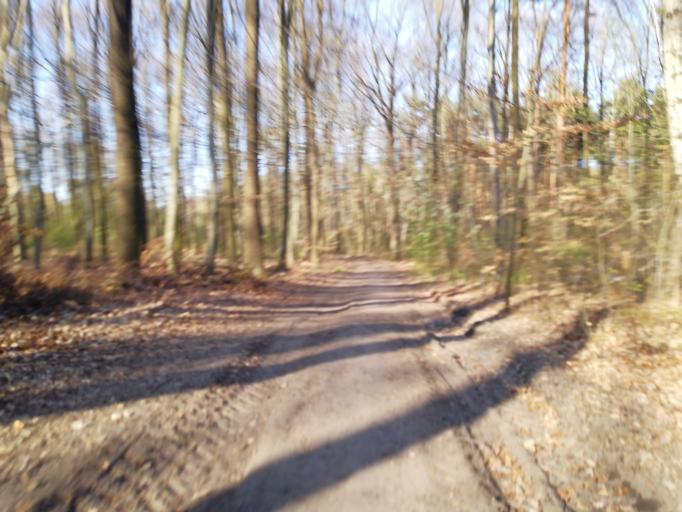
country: DE
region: Brandenburg
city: Calau
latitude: 51.7208
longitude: 13.9566
